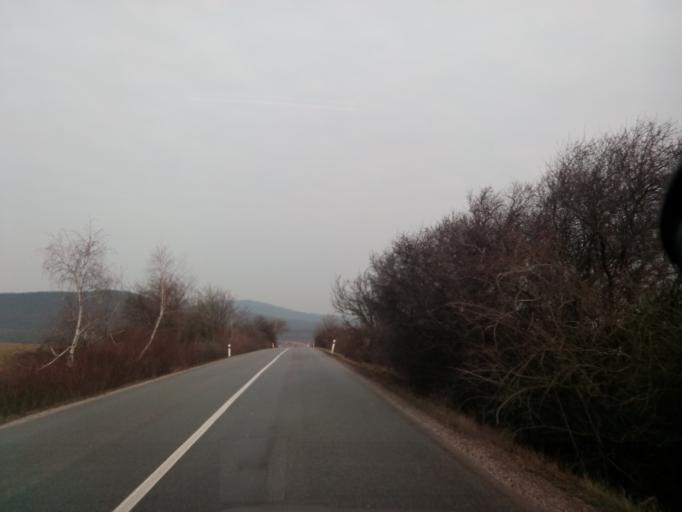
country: SK
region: Kosicky
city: Secovce
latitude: 48.6321
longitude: 21.5546
